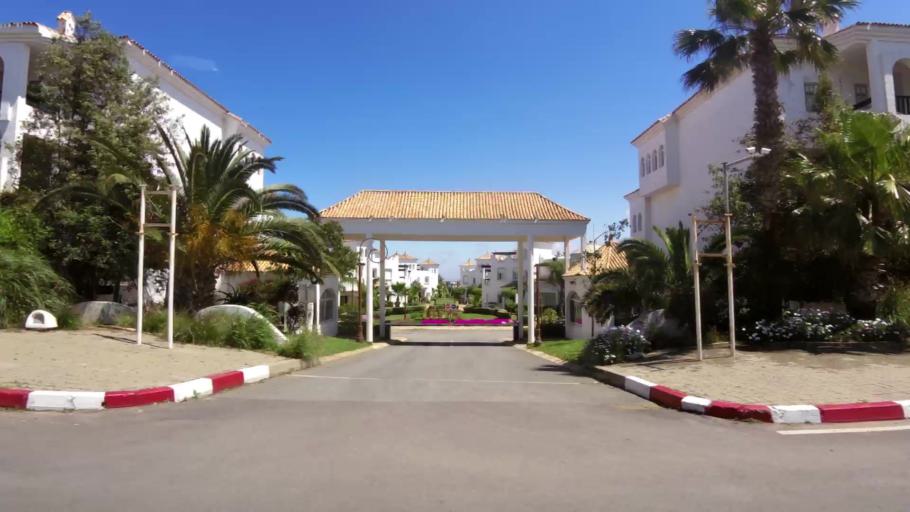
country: MA
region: Grand Casablanca
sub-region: Nouaceur
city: Dar Bouazza
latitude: 33.5286
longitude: -7.8203
